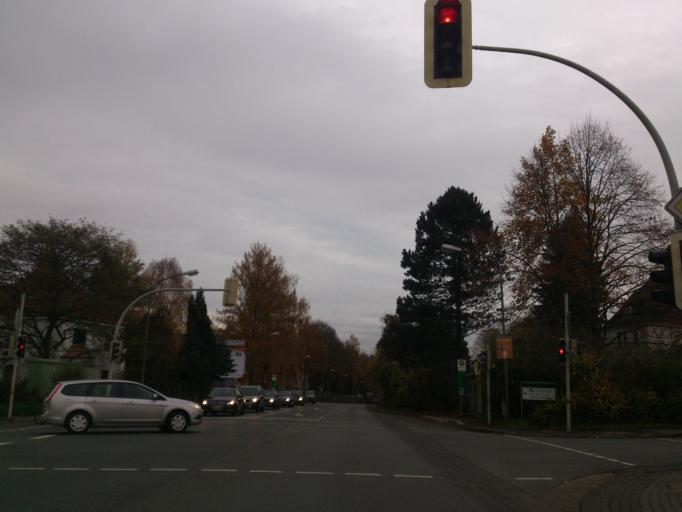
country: DE
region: North Rhine-Westphalia
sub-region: Regierungsbezirk Detmold
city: Hoexter
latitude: 51.7832
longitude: 9.3711
